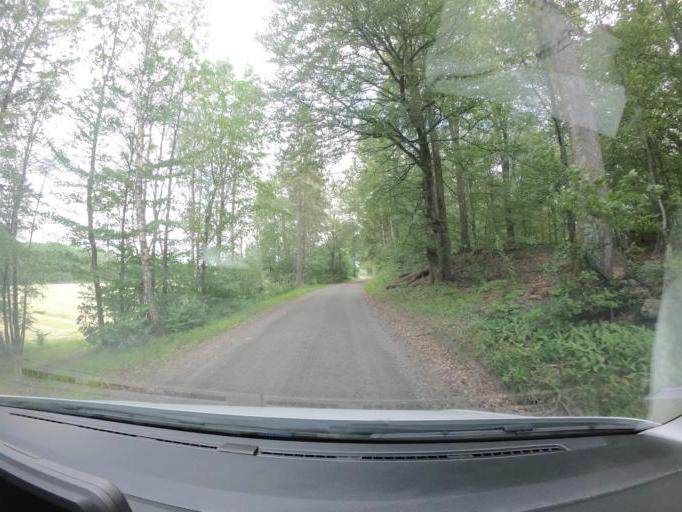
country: SE
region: Skane
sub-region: Hassleholms Kommun
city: Sosdala
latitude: 56.0601
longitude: 13.6552
